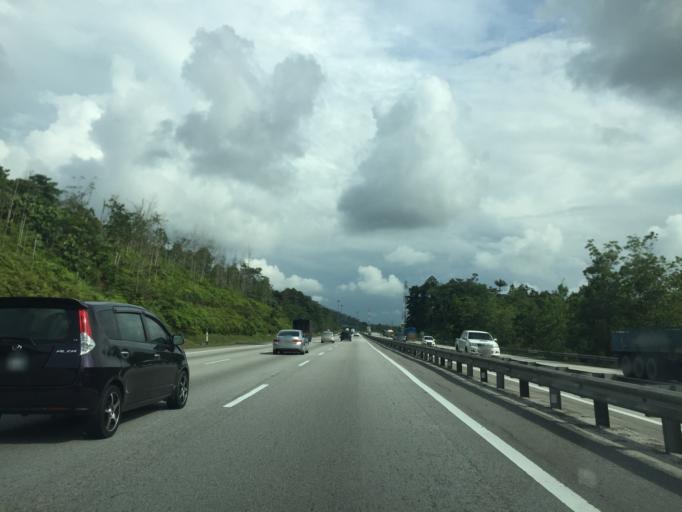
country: MY
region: Selangor
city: Batang Berjuntai
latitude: 3.5689
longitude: 101.5228
